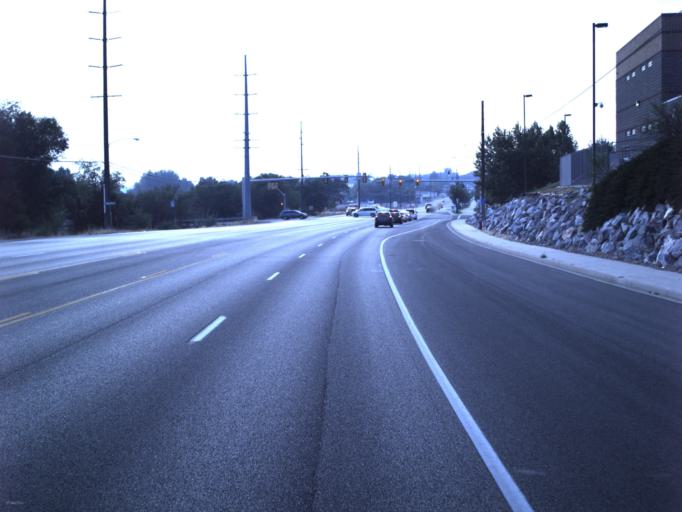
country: US
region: Utah
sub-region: Utah County
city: Provo
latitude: 40.2067
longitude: -111.6286
